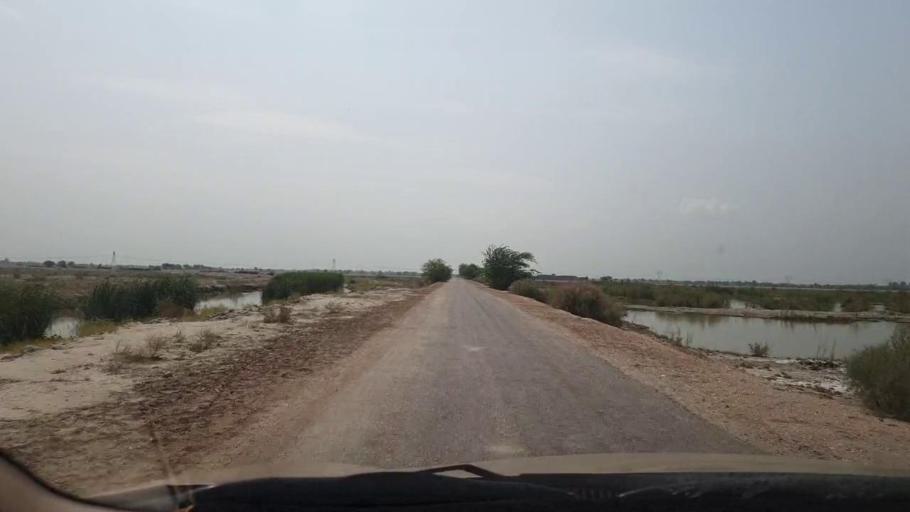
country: PK
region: Sindh
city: Goth Garelo
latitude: 27.5007
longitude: 68.1154
